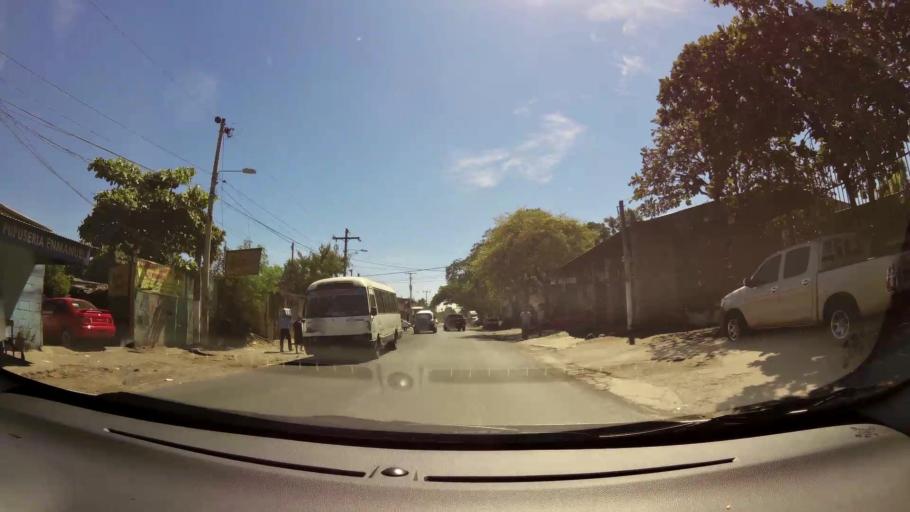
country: SV
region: San Salvador
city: Apopa
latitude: 13.7999
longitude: -89.1811
